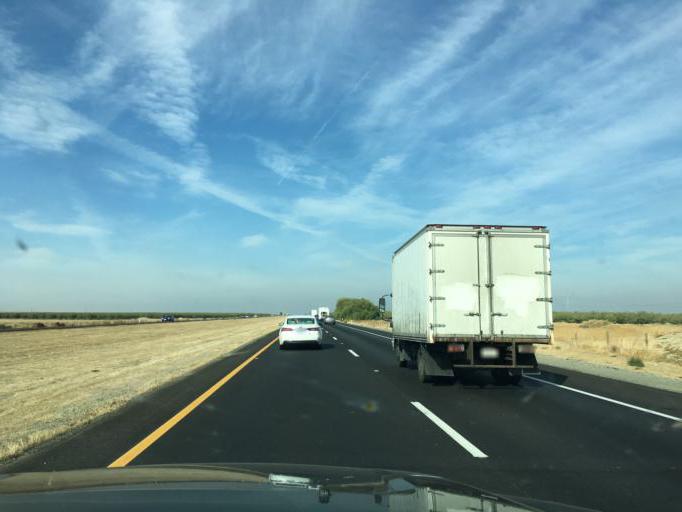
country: US
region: California
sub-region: Fresno County
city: Huron
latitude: 36.2736
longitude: -120.2560
